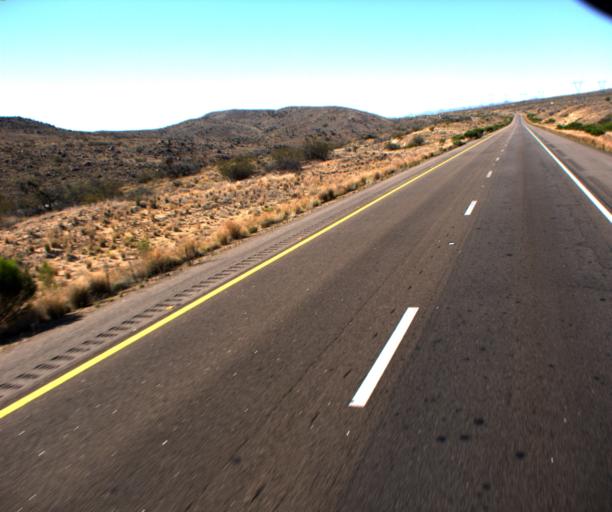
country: US
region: Arizona
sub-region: Mohave County
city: Kingman
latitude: 34.9756
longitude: -113.6694
